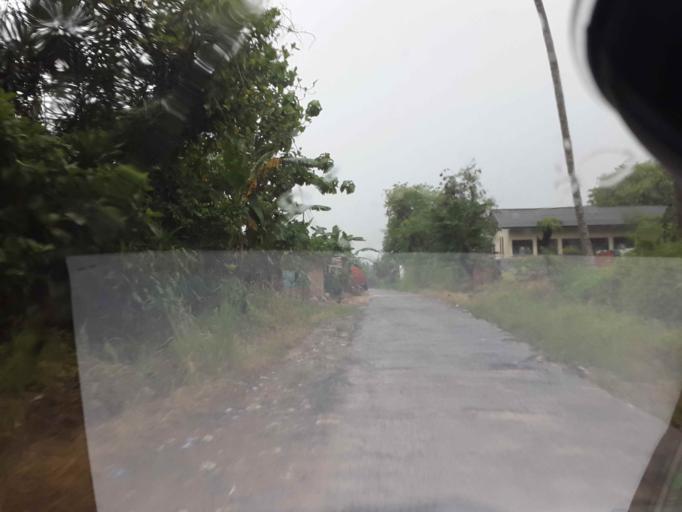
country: ID
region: Lampung
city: Panjang
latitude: -5.3952
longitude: 105.3529
